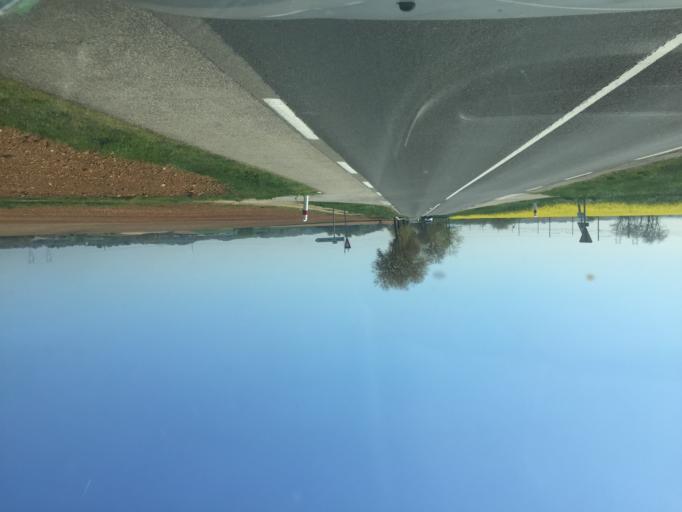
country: FR
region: Rhone-Alpes
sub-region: Departement de l'Ain
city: Perouges
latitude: 45.8775
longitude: 5.1615
